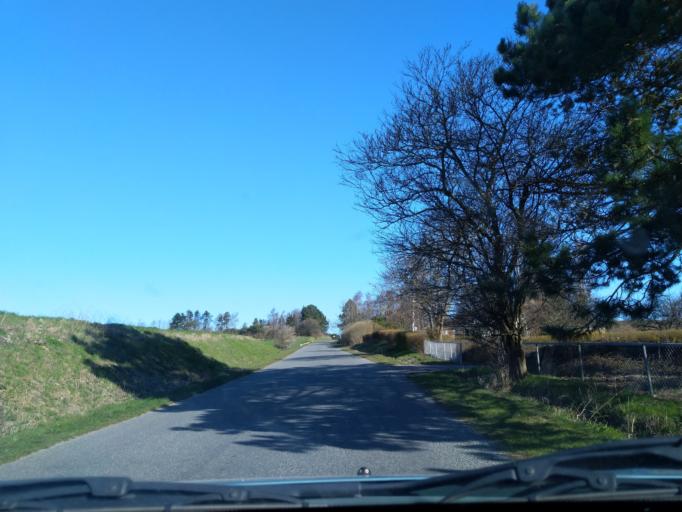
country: DK
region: Zealand
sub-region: Kalundborg Kommune
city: Kalundborg
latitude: 55.7349
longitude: 10.9580
